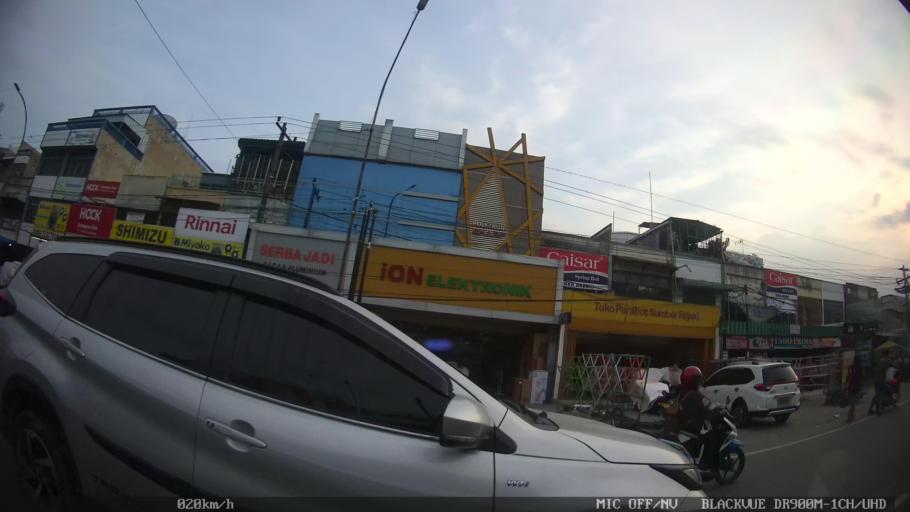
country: ID
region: North Sumatra
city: Sunggal
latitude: 3.5989
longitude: 98.6067
